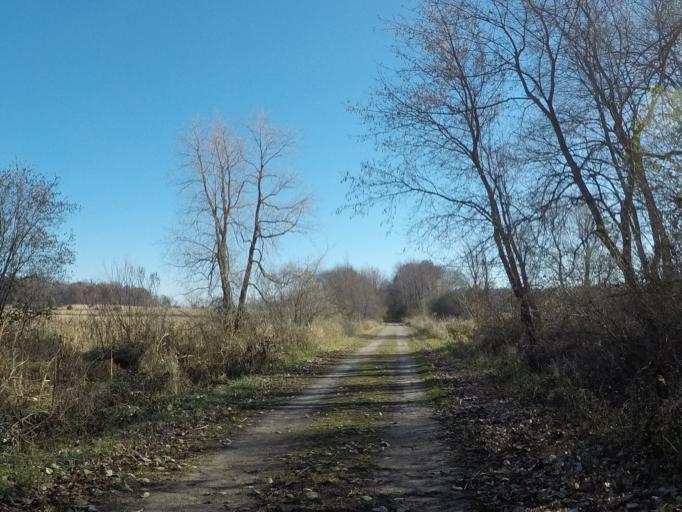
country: US
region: Wisconsin
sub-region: Jefferson County
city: Cambridge
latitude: 43.0434
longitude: -89.0271
